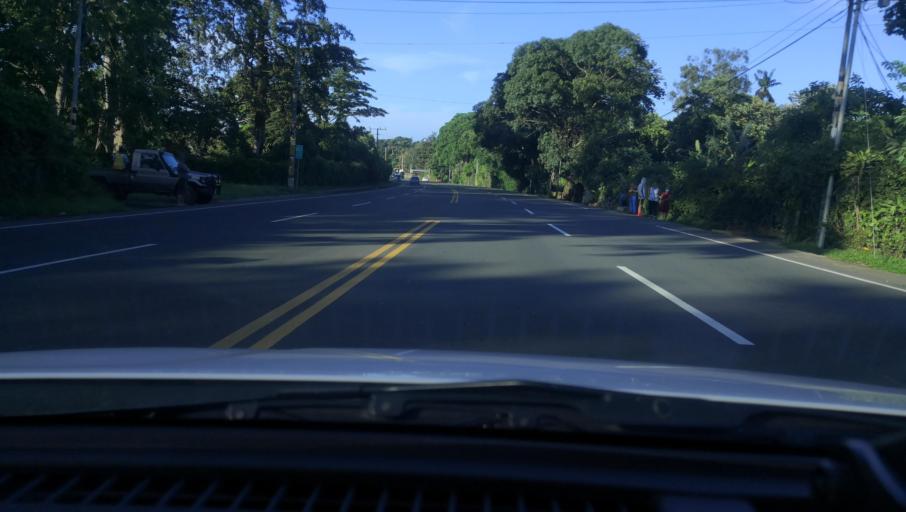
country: NI
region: Carazo
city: Diriamba
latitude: 11.8747
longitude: -86.2382
